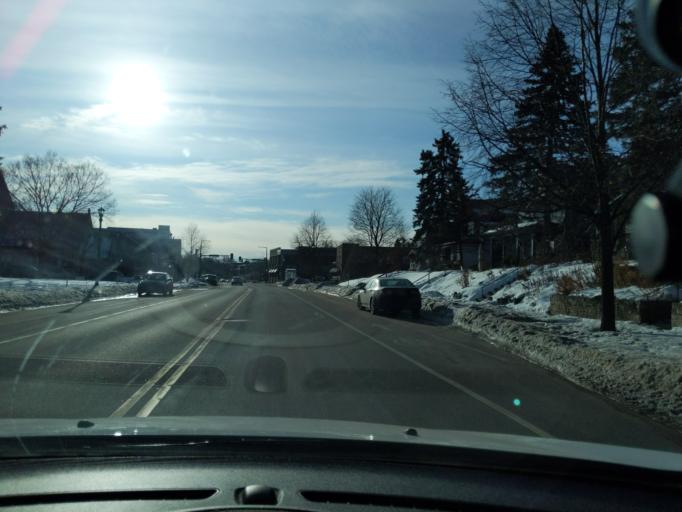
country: US
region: Minnesota
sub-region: Ramsey County
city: Lauderdale
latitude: 44.9834
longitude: -93.1968
